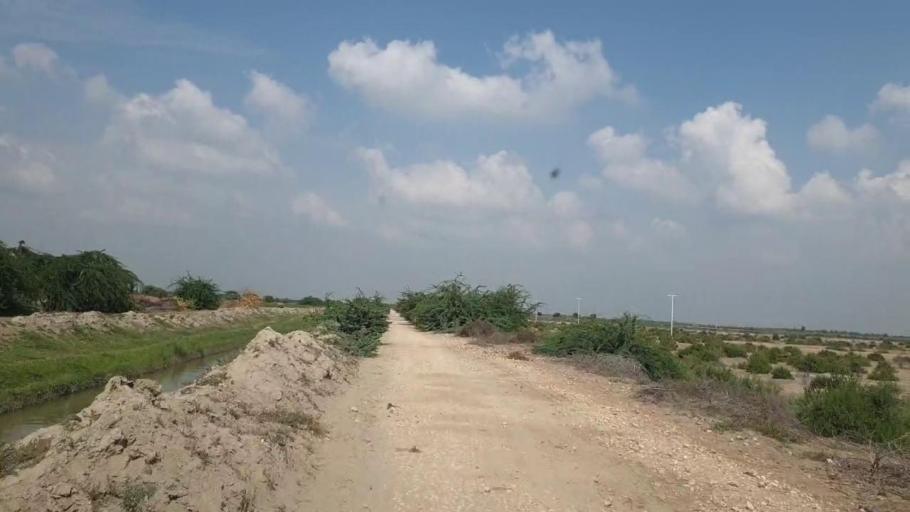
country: PK
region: Sindh
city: Badin
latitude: 24.4996
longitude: 68.6557
